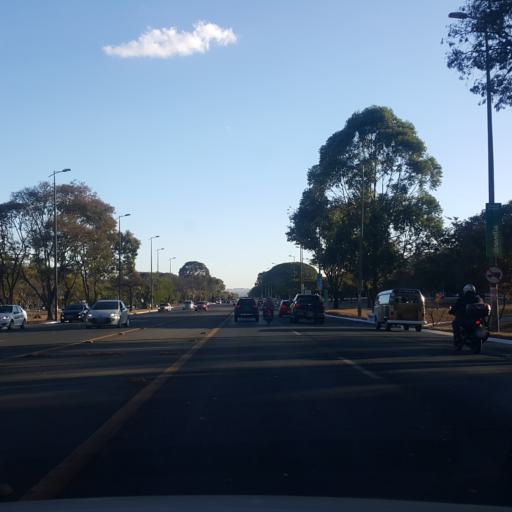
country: BR
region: Federal District
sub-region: Brasilia
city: Brasilia
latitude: -15.8247
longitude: -47.9115
